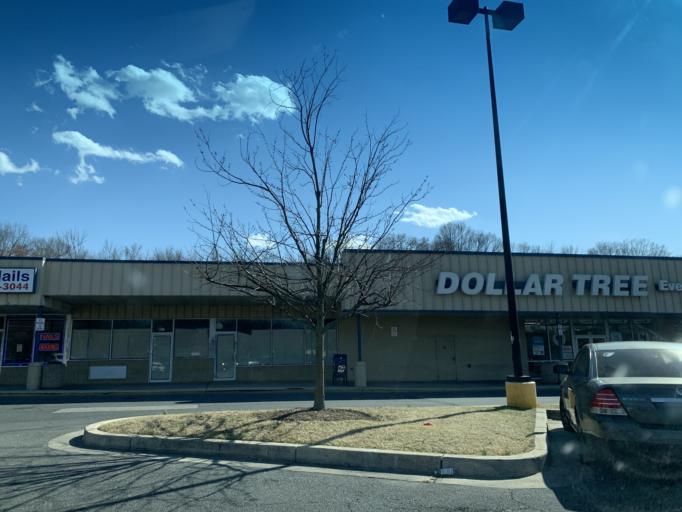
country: US
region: Maryland
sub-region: Baltimore County
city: Bowleys Quarters
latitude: 39.3362
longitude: -76.3995
